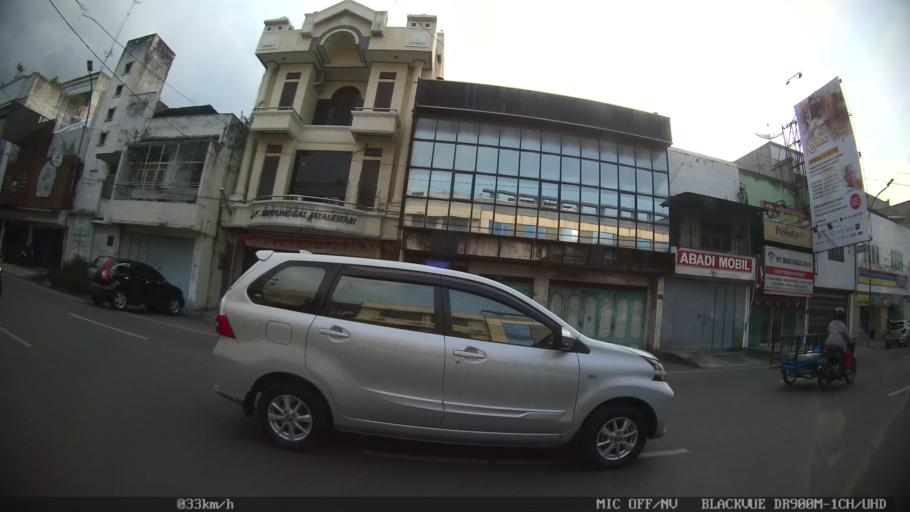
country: ID
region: North Sumatra
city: Medan
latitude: 3.5933
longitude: 98.6820
